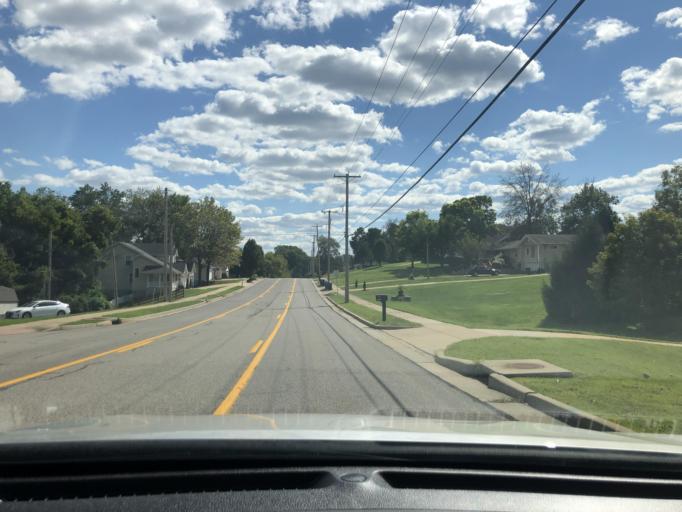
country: US
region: Missouri
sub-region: Saint Louis County
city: Green Park
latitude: 38.5102
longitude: -90.3429
